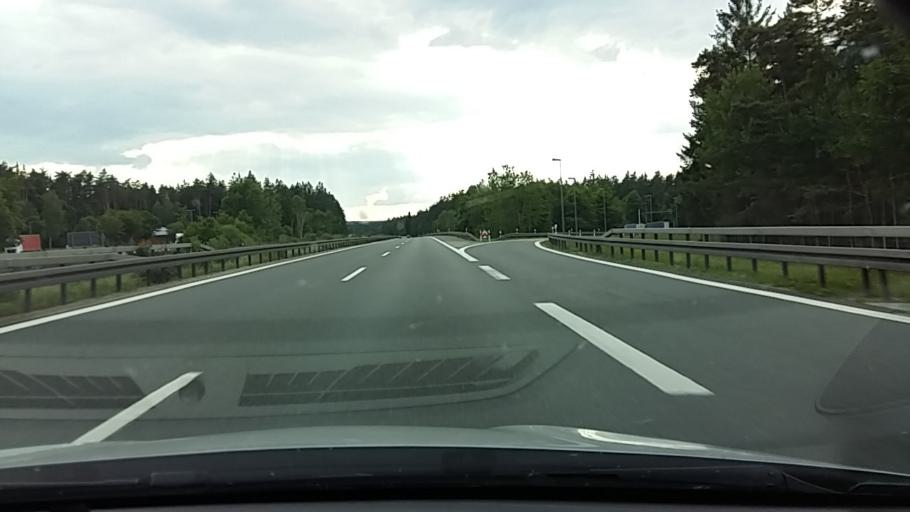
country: DE
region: Bavaria
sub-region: Upper Palatinate
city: Kummersbruck
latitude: 49.3960
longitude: 11.8629
